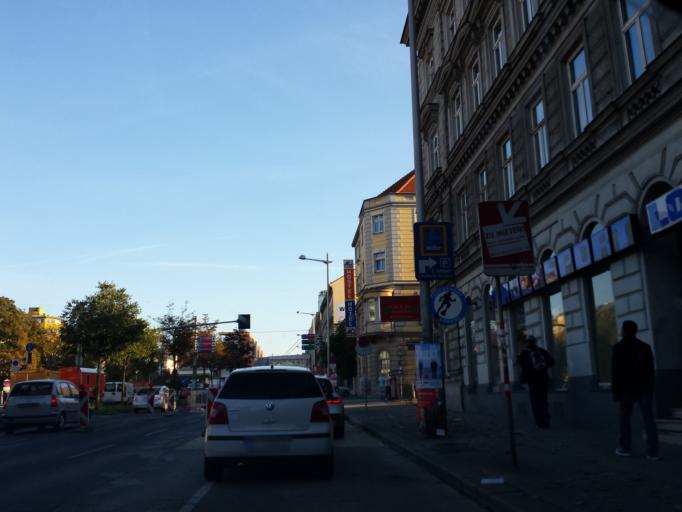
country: AT
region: Vienna
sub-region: Wien Stadt
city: Vienna
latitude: 48.2058
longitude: 16.3366
